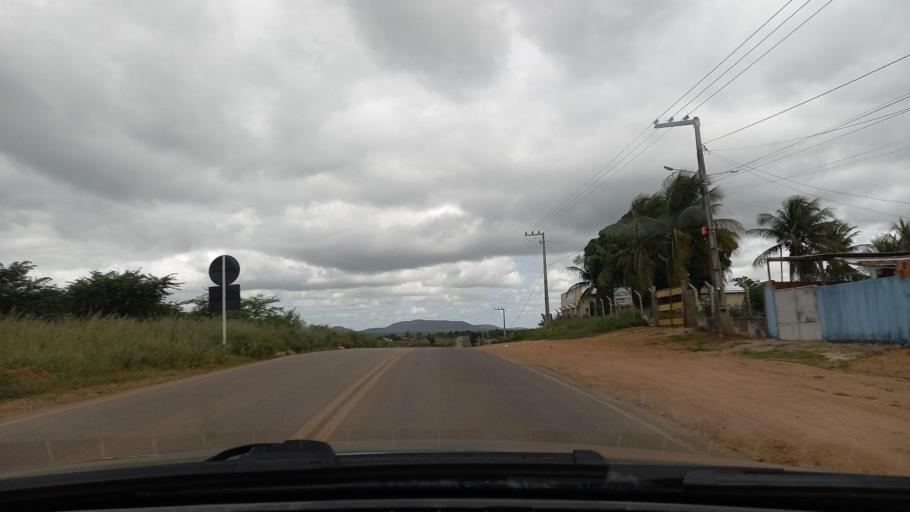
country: BR
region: Sergipe
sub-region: Caninde De Sao Francisco
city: Caninde de Sao Francisco
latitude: -9.6699
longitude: -37.7982
